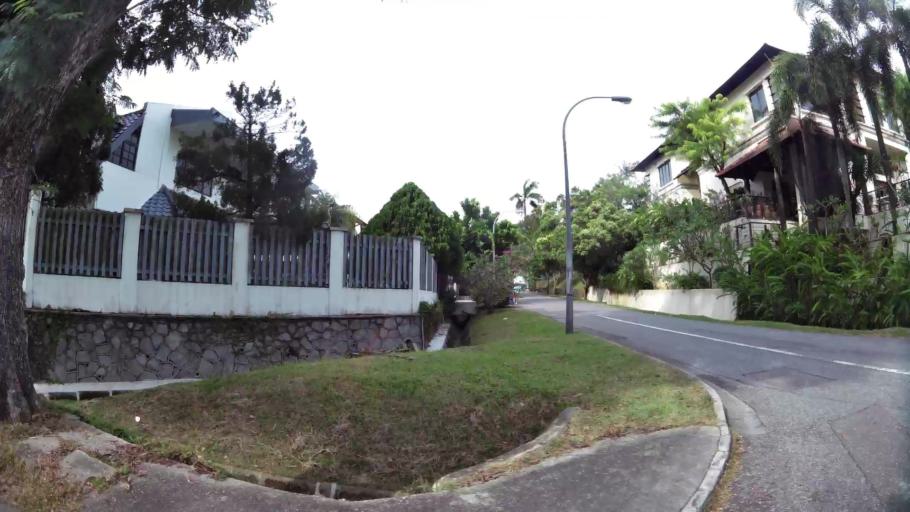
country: SG
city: Singapore
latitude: 1.3234
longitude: 103.8207
